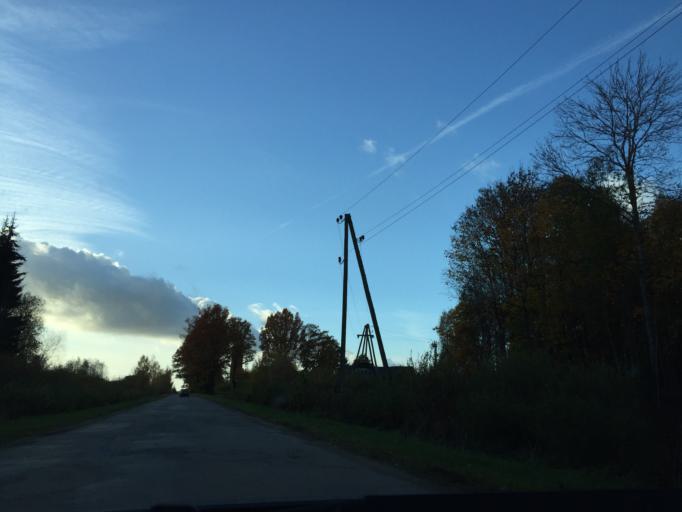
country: LV
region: Ogre
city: Jumprava
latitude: 56.7671
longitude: 25.0084
